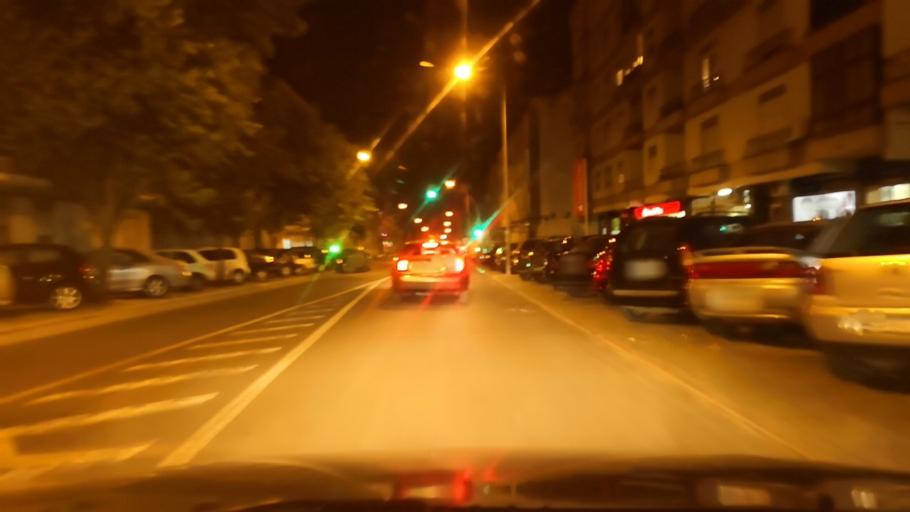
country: PT
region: Setubal
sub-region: Setubal
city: Setubal
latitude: 38.5368
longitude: -8.8941
